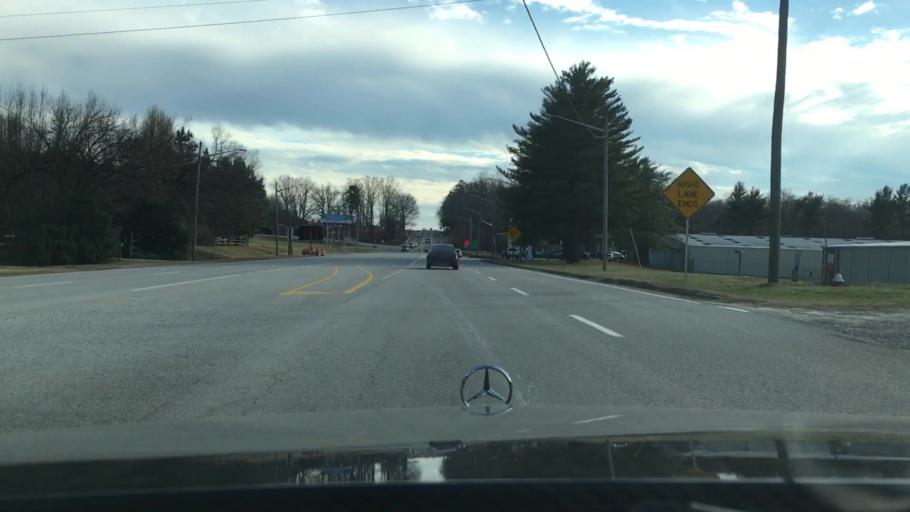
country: US
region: Virginia
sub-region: City of Danville
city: Danville
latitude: 36.5435
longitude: -79.4011
